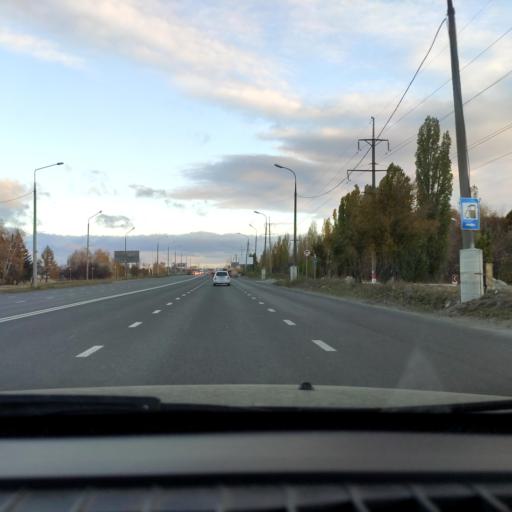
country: RU
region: Samara
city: Tol'yatti
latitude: 53.5577
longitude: 49.2888
